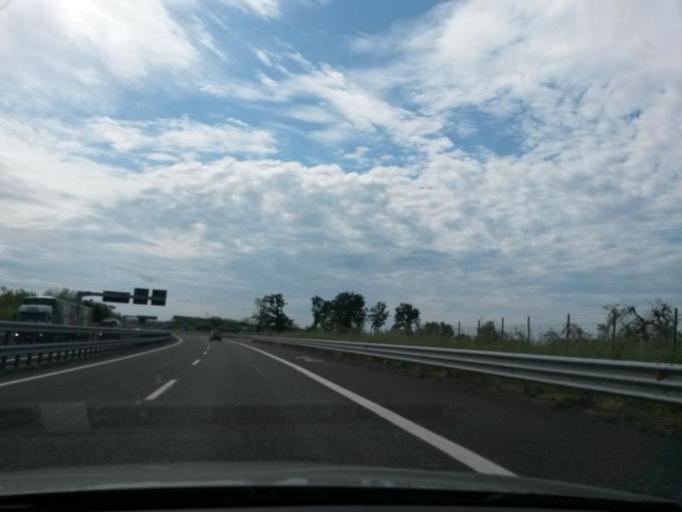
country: IT
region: Tuscany
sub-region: Provincia di Livorno
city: S.P. in Palazzi
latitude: 43.3633
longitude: 10.5064
